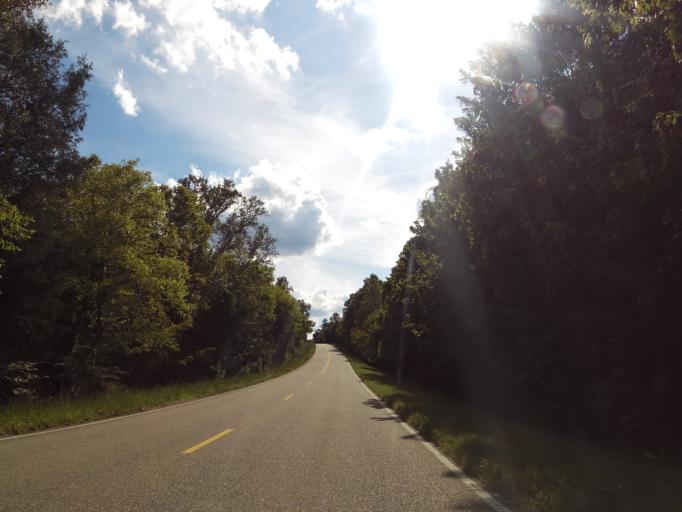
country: US
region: Alabama
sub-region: Dallas County
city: Selmont-West Selmont
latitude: 32.1786
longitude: -87.0466
